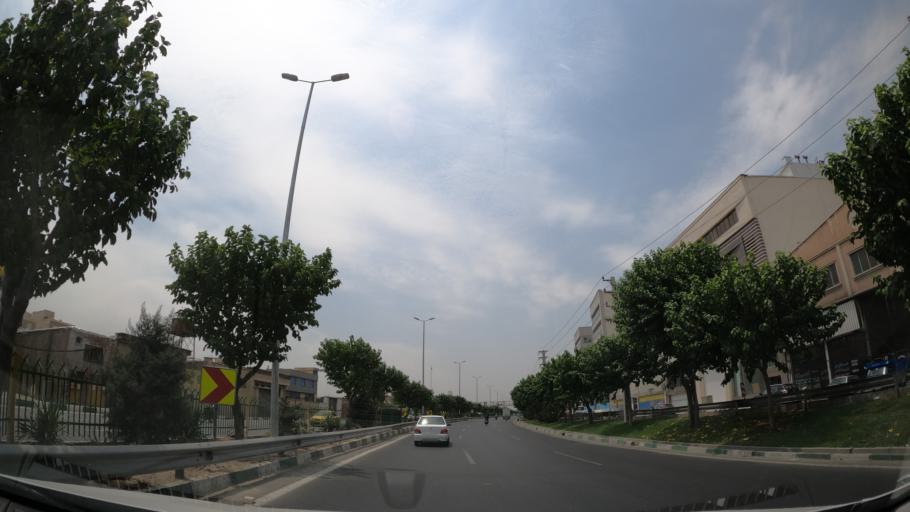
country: IR
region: Tehran
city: Tehran
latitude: 35.6750
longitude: 51.3247
